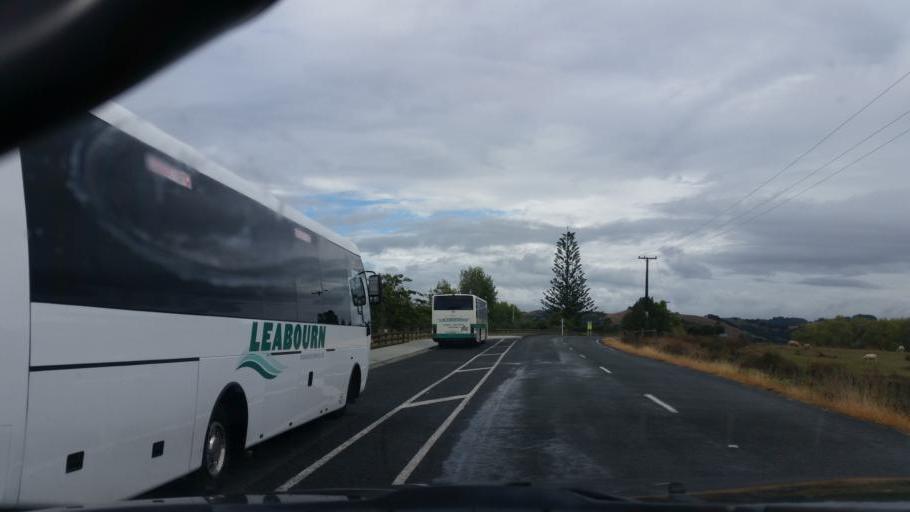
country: NZ
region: Northland
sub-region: Whangarei
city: Ruakaka
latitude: -36.1158
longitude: 174.3654
